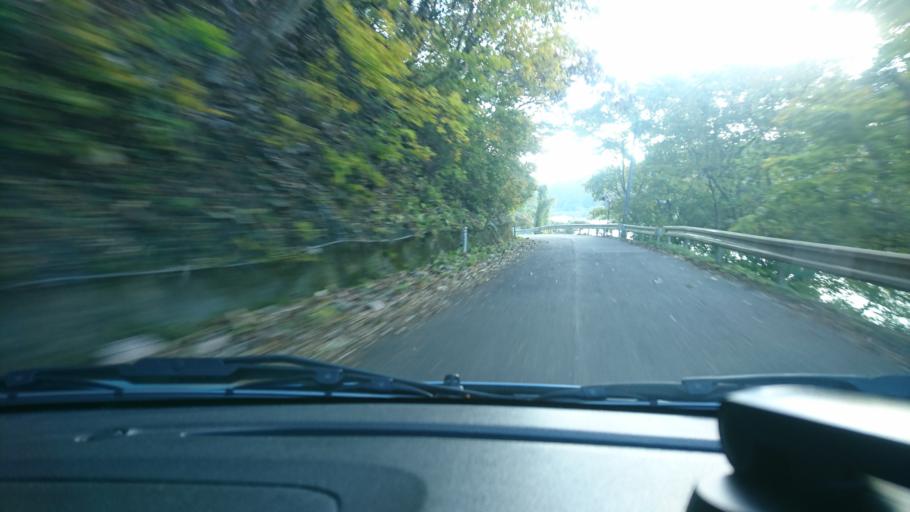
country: JP
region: Iwate
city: Ichinoseki
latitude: 38.8124
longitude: 141.2522
